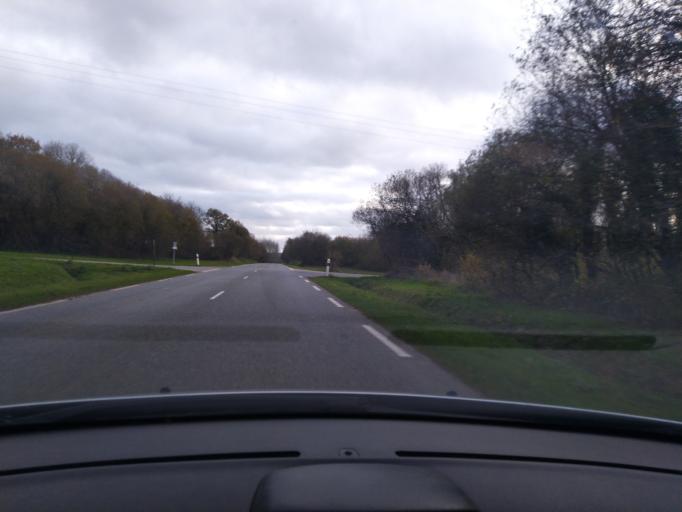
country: FR
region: Brittany
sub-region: Departement des Cotes-d'Armor
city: Plouaret
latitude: 48.5890
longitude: -3.4957
